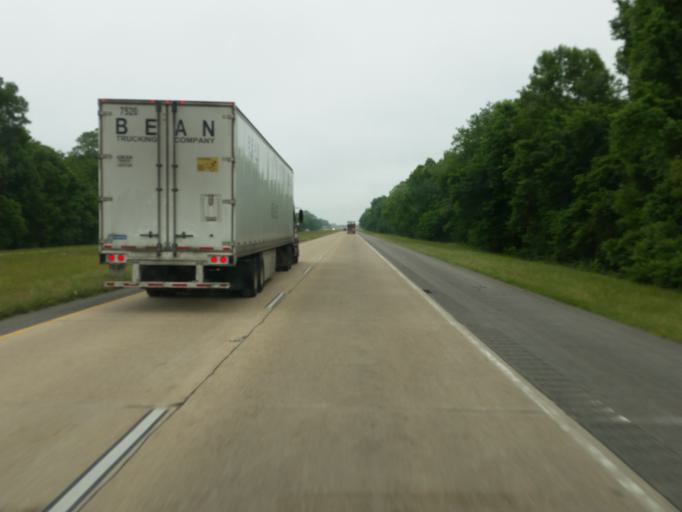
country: US
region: Louisiana
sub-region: Madison Parish
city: Tallulah
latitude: 32.3716
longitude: -91.1444
